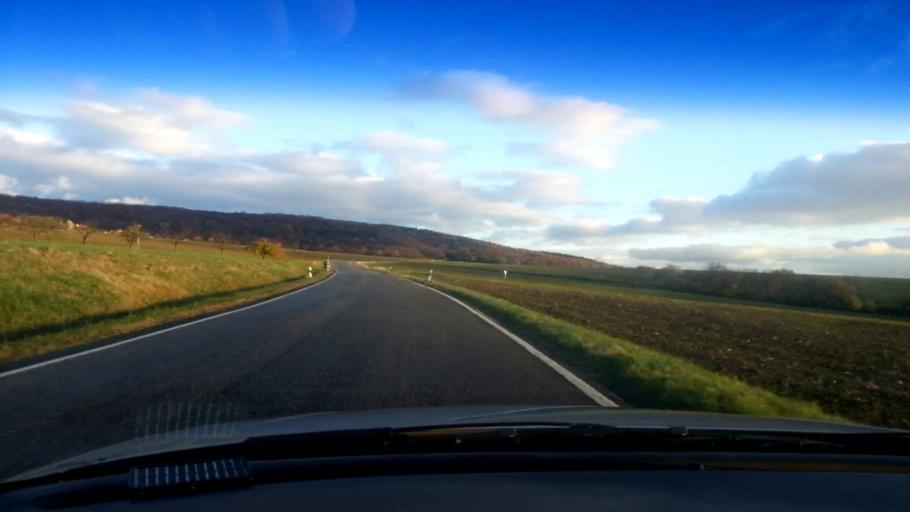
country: DE
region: Bavaria
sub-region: Upper Franconia
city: Buttenheim
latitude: 49.8431
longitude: 11.0220
